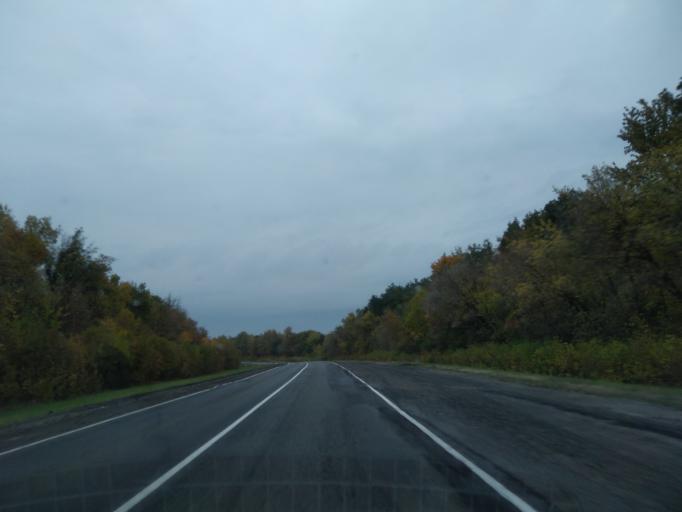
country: RU
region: Lipetsk
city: Zadonsk
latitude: 52.5166
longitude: 38.7581
